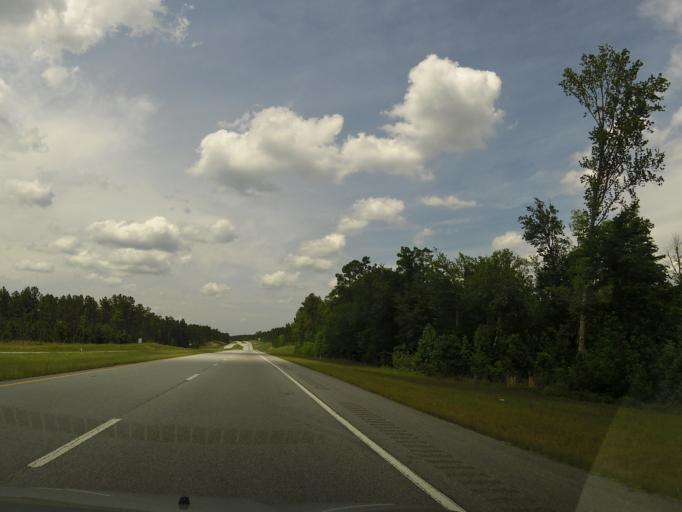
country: US
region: Georgia
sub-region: Emanuel County
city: Swainsboro
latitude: 32.6996
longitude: -82.3907
